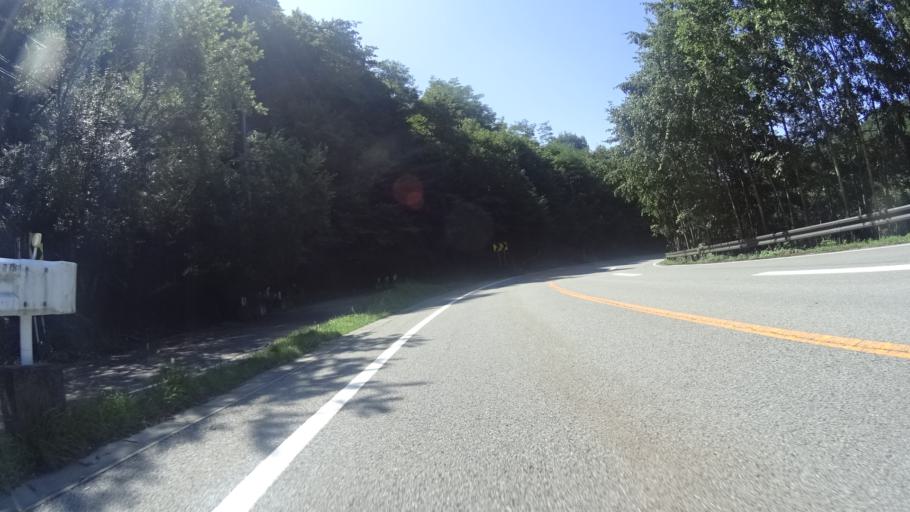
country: JP
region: Yamanashi
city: Enzan
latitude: 35.7622
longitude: 138.8071
